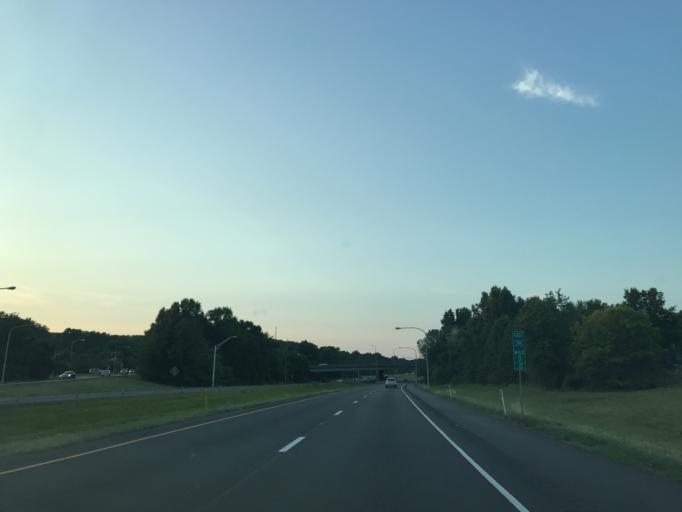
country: US
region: Pennsylvania
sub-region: Bucks County
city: Langhorne Manor
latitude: 40.1632
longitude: -74.9002
